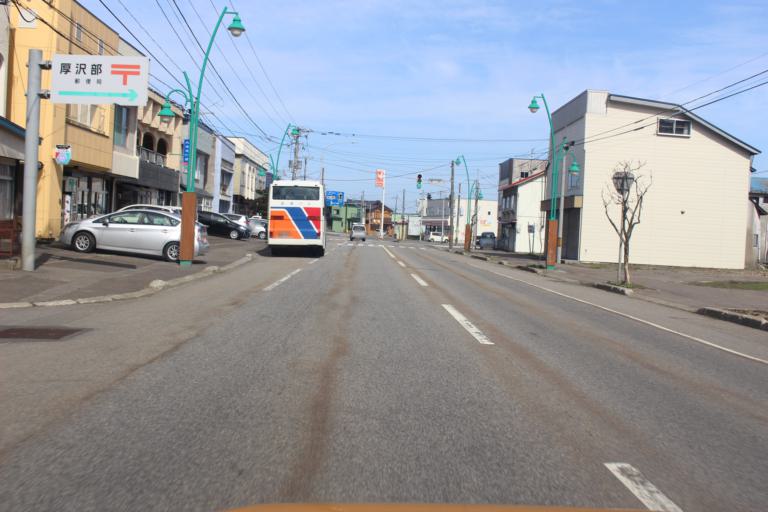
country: JP
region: Hokkaido
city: Kamiiso
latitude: 41.9162
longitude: 140.2246
